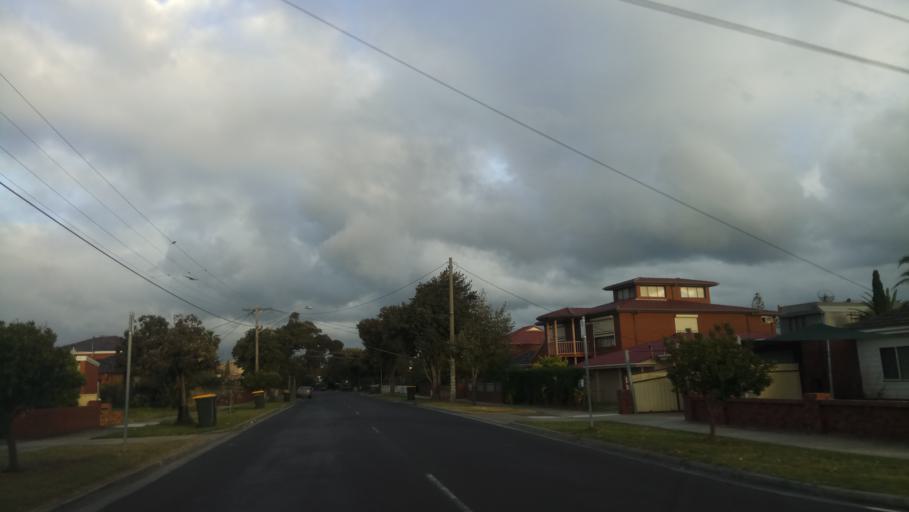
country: AU
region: Victoria
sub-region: Hobsons Bay
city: Altona
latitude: -37.8698
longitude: 144.8328
